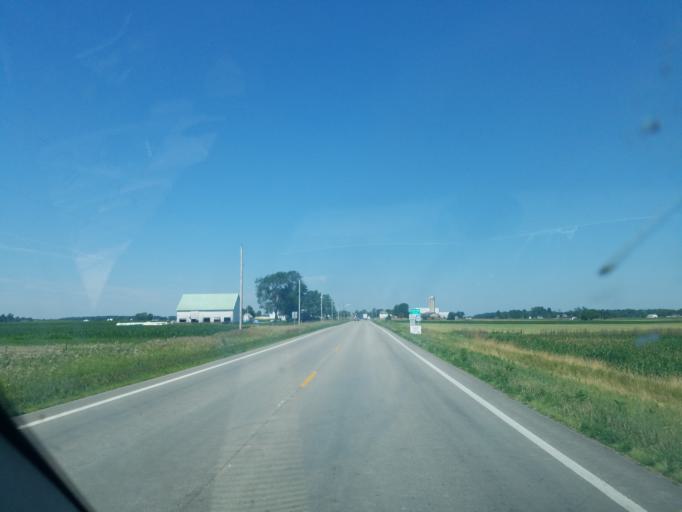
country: US
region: Ohio
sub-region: Shelby County
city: Botkins
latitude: 40.4389
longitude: -84.2494
